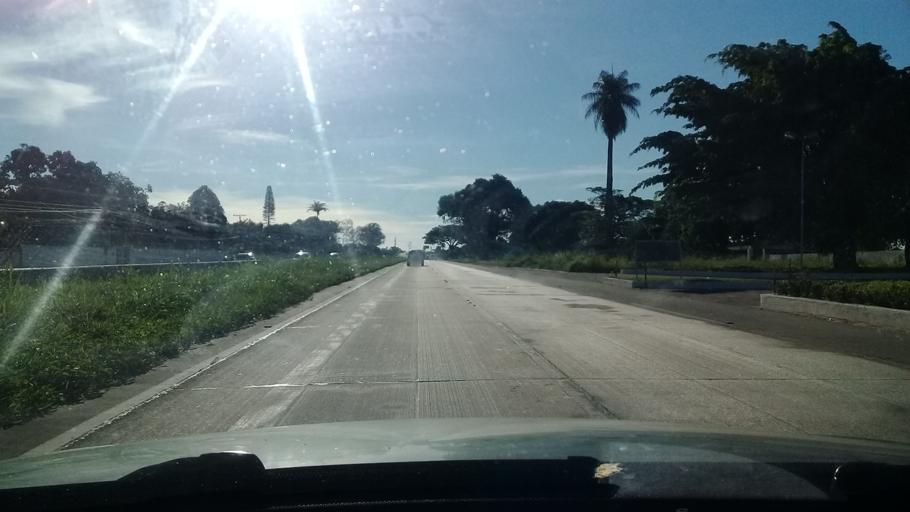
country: BR
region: Pernambuco
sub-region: Carpina
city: Carpina
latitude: -7.8579
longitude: -35.2166
